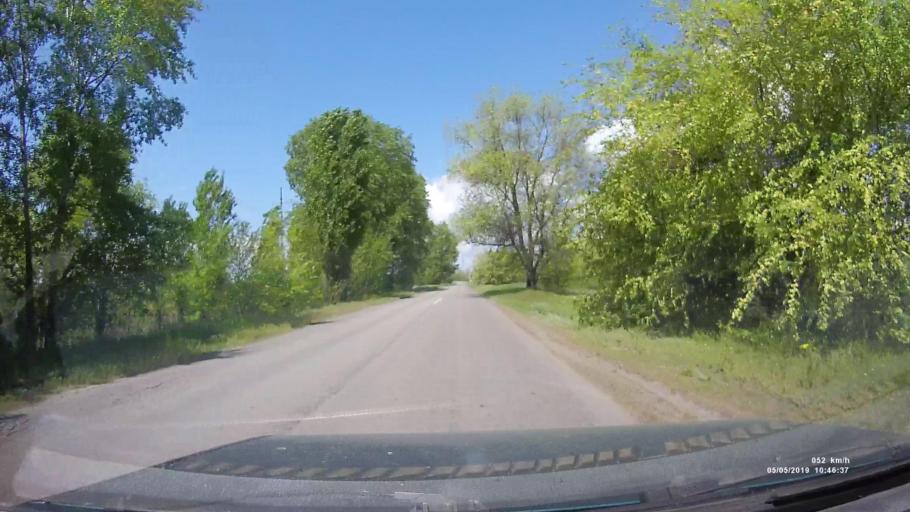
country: RU
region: Rostov
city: Ust'-Donetskiy
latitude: 47.6351
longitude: 40.8425
